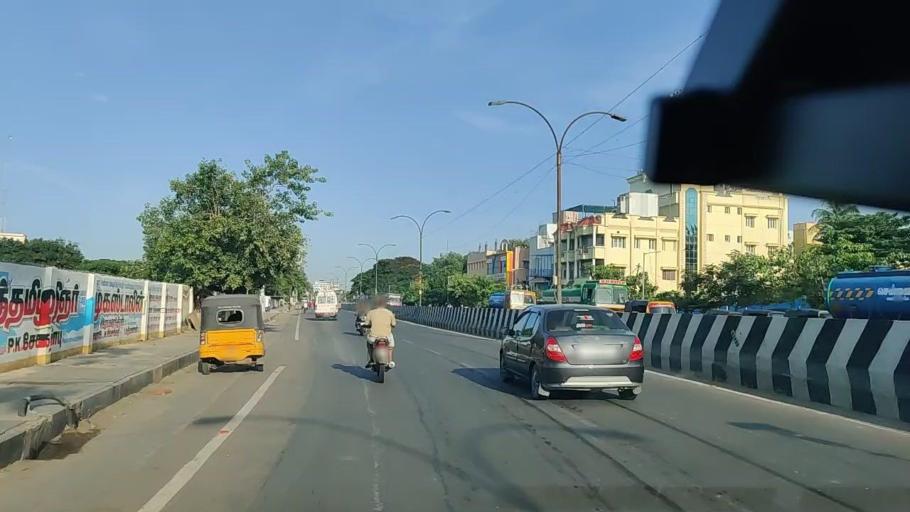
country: IN
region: Tamil Nadu
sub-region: Chennai
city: George Town
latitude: 13.1179
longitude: 80.2615
